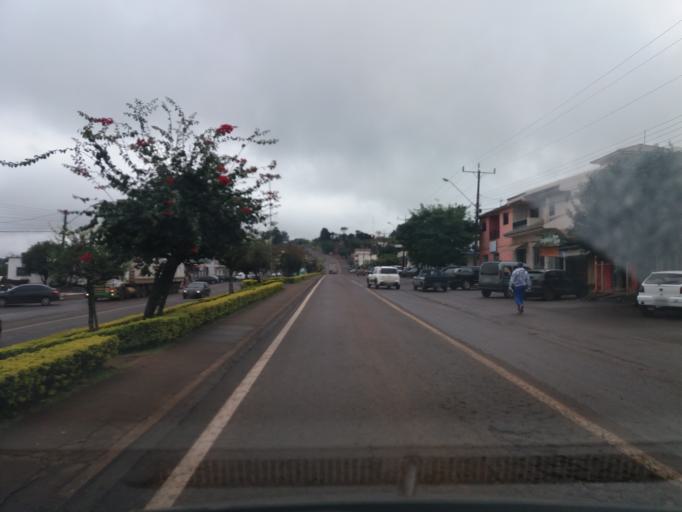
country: BR
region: Parana
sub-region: Cascavel
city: Cascavel
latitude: -25.2587
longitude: -53.5761
